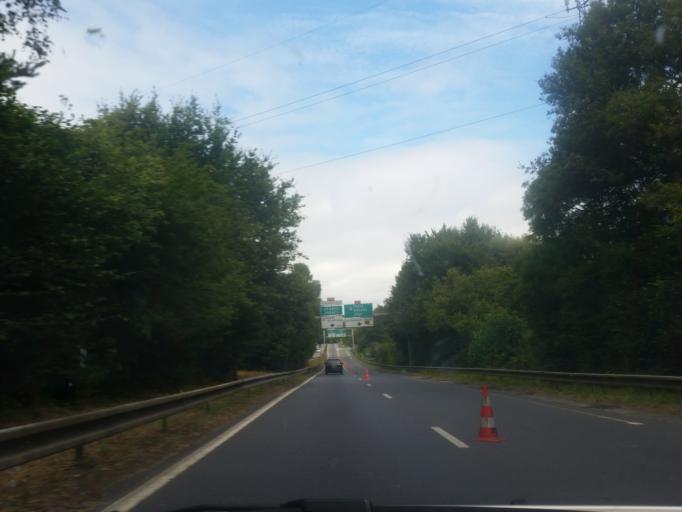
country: FR
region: Pays de la Loire
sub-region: Departement de la Loire-Atlantique
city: La Chapelle-sur-Erdre
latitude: 47.2648
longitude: -1.5593
